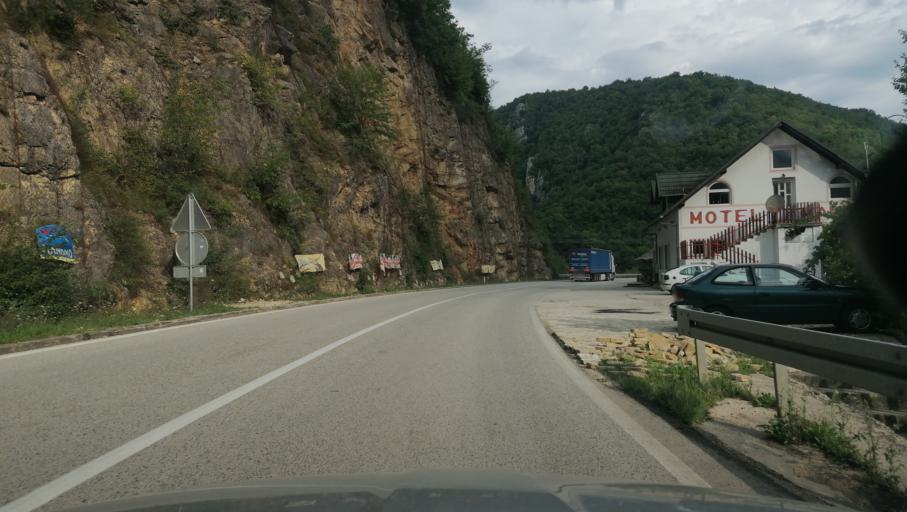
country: BA
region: Republika Srpska
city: Mrkonjic Grad
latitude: 44.4656
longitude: 17.1791
